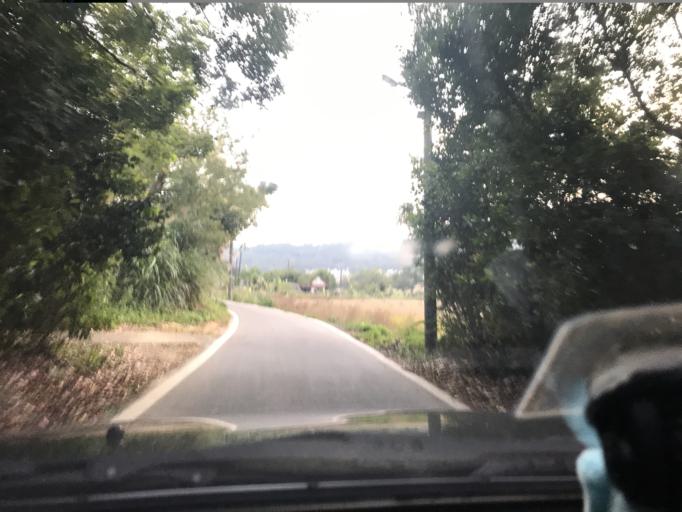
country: TW
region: Taiwan
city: Daxi
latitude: 24.8545
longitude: 121.2111
